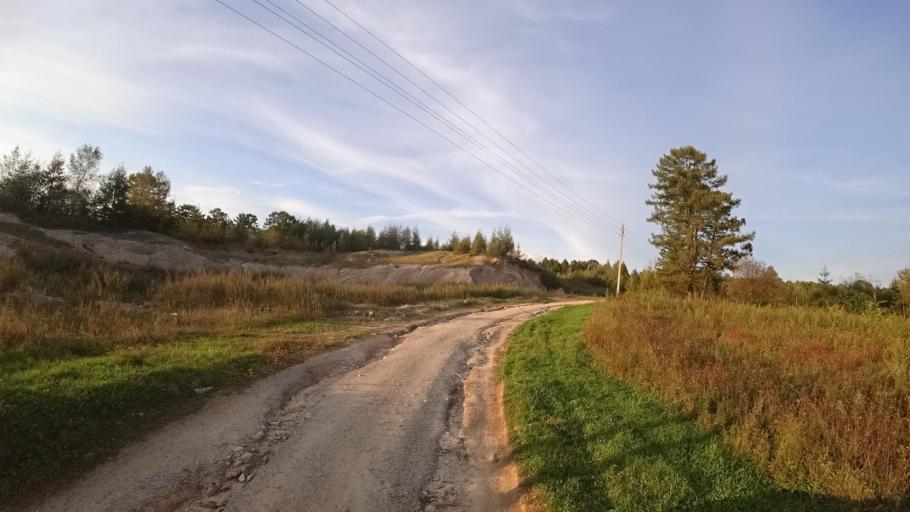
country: RU
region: Jewish Autonomous Oblast
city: Kul'dur
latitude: 49.2088
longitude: 131.6467
